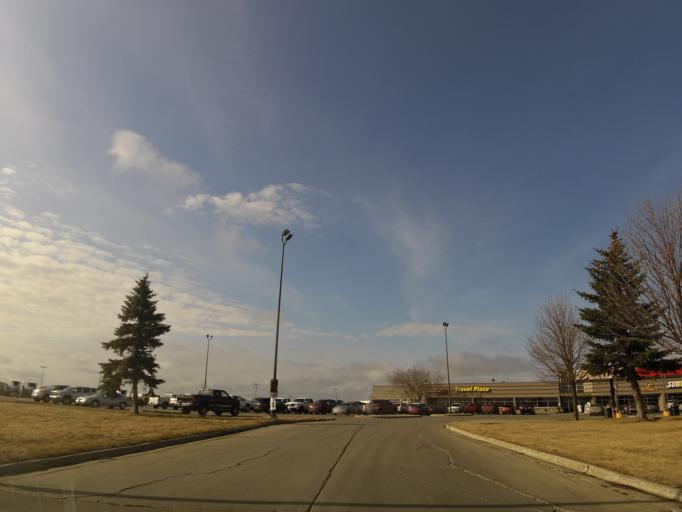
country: US
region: North Dakota
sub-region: Grand Forks County
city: Grand Forks
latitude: 47.8887
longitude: -97.0916
